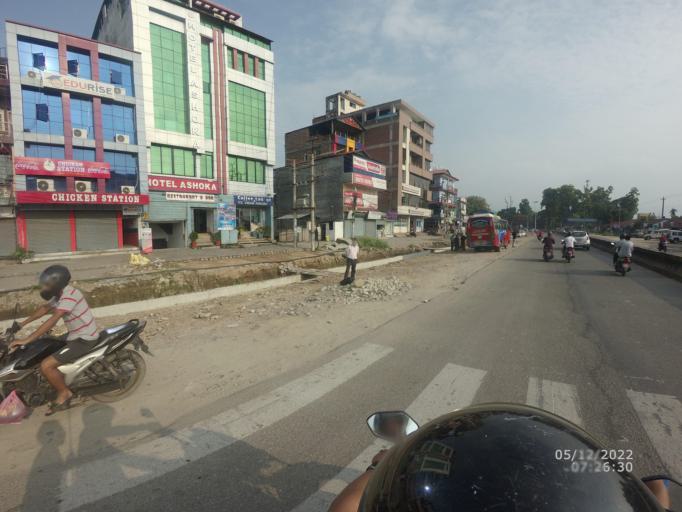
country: NP
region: Central Region
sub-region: Narayani Zone
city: Bharatpur
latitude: 27.6850
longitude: 84.4296
